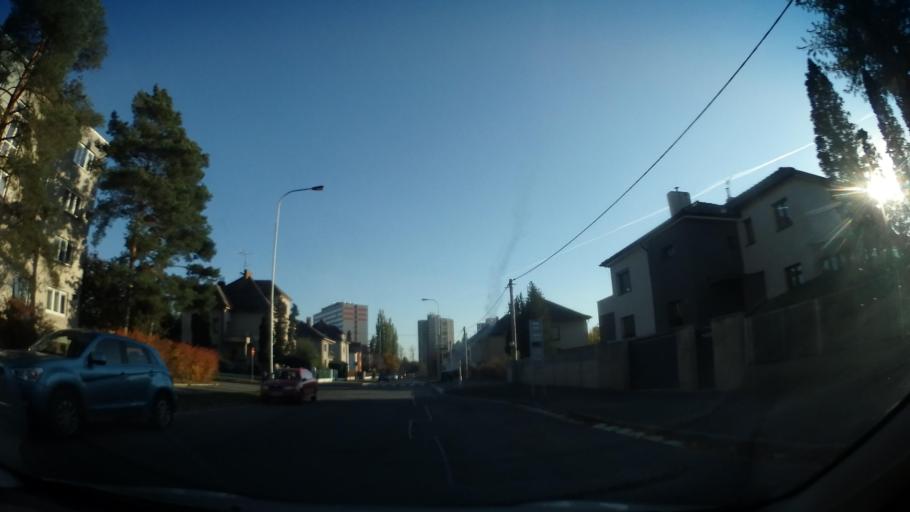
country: CZ
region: Kralovehradecky
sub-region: Okres Hradec Kralove
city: Hradec Kralove
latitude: 50.2032
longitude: 15.8151
